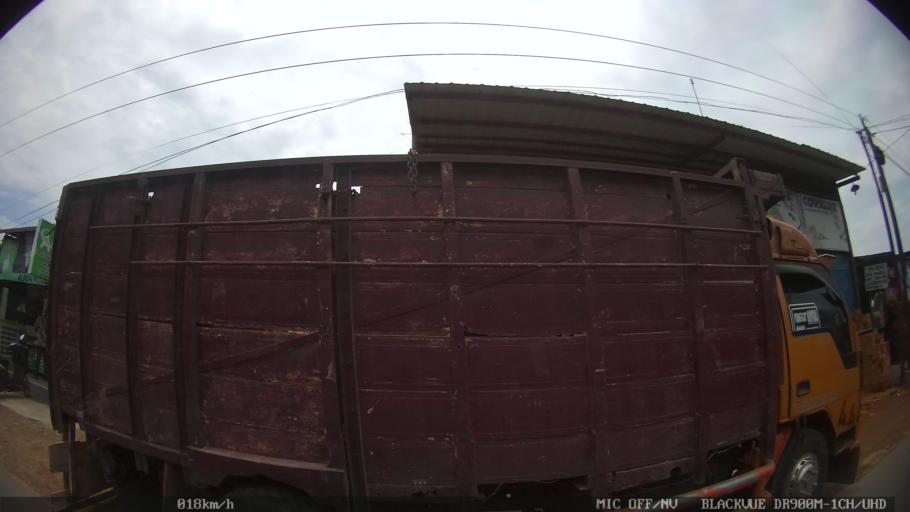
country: ID
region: North Sumatra
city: Sunggal
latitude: 3.6094
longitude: 98.5802
